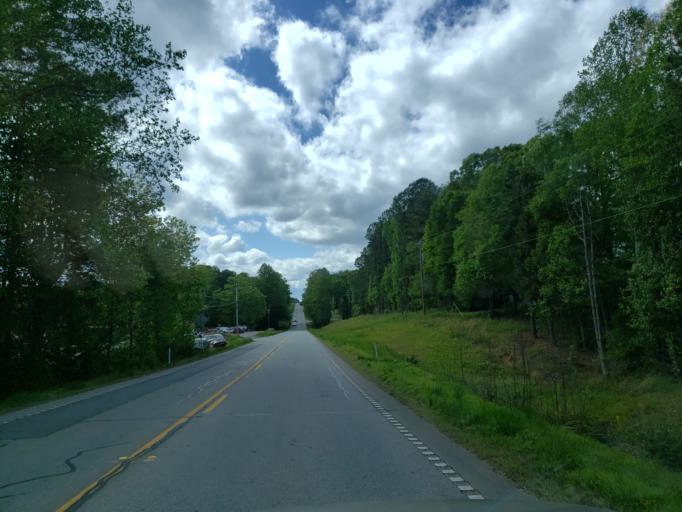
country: US
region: Georgia
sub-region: Haralson County
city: Bremen
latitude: 33.7059
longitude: -85.1949
